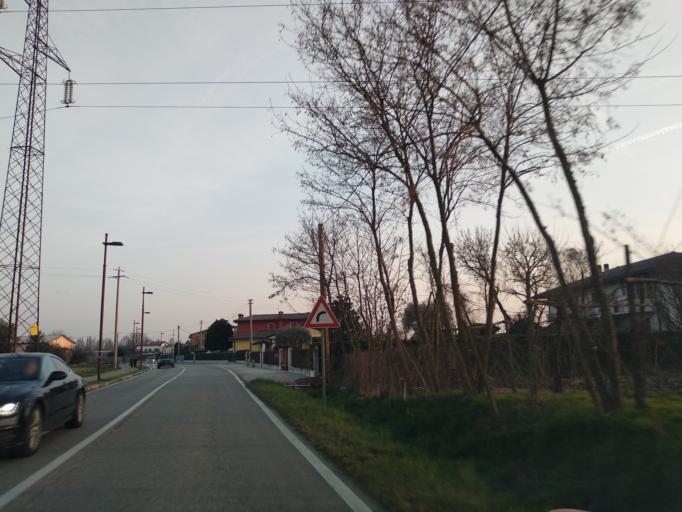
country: IT
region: Veneto
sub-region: Provincia di Padova
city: Sarmeola
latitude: 45.4334
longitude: 11.8081
